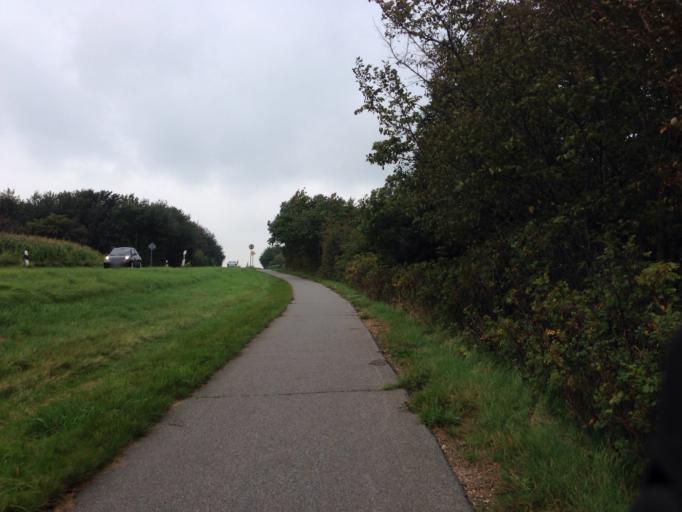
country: DE
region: Schleswig-Holstein
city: Oevenum
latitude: 54.7049
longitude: 8.5336
